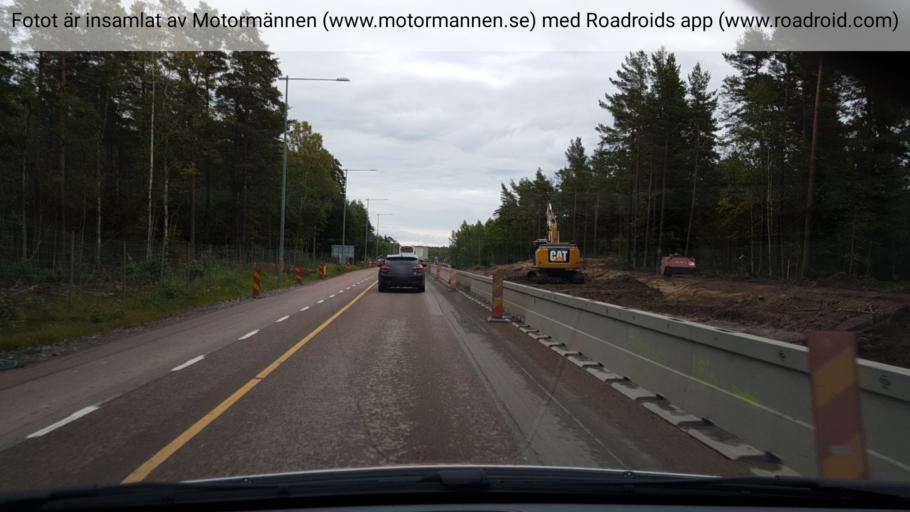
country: SE
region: Vaermland
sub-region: Hammaro Kommun
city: Skoghall
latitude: 59.3810
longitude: 13.4009
